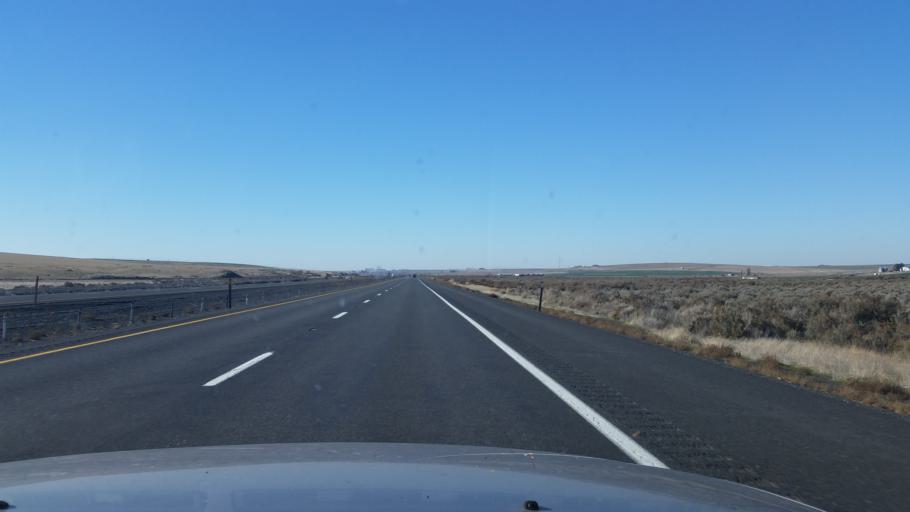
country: US
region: Washington
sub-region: Grant County
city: Warden
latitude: 47.0846
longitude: -118.9868
